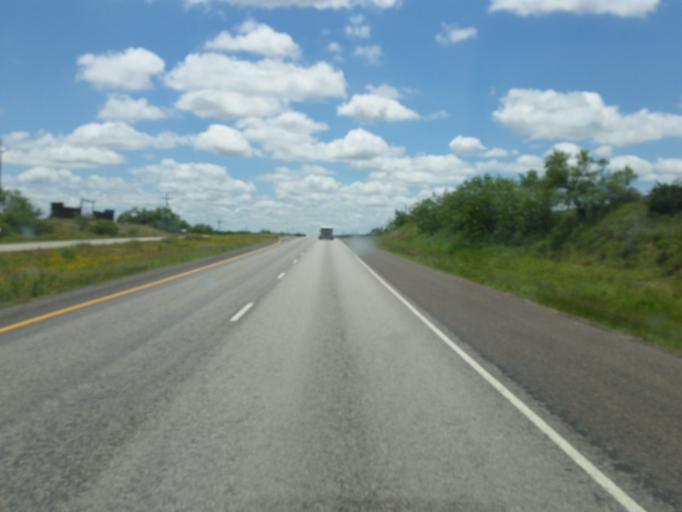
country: US
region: Texas
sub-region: Garza County
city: Post
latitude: 33.0378
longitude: -101.1981
